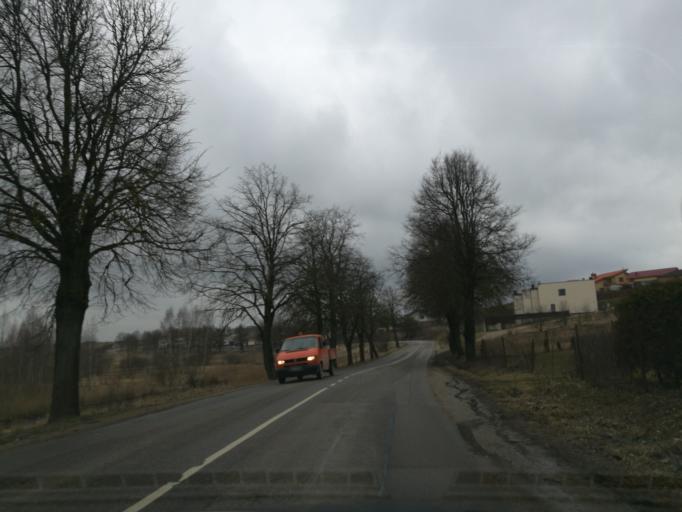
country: LT
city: Grigiskes
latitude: 54.6452
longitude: 25.0964
